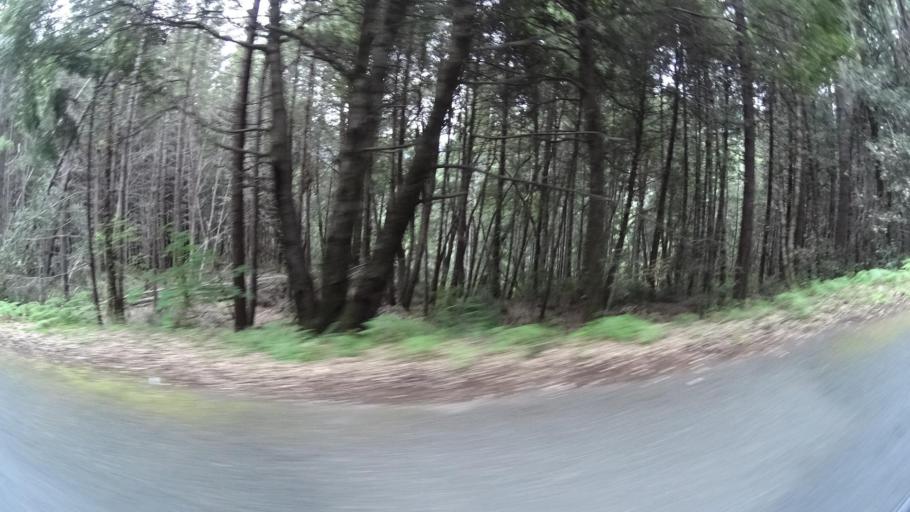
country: US
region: California
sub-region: Humboldt County
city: Willow Creek
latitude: 41.2001
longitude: -123.7556
